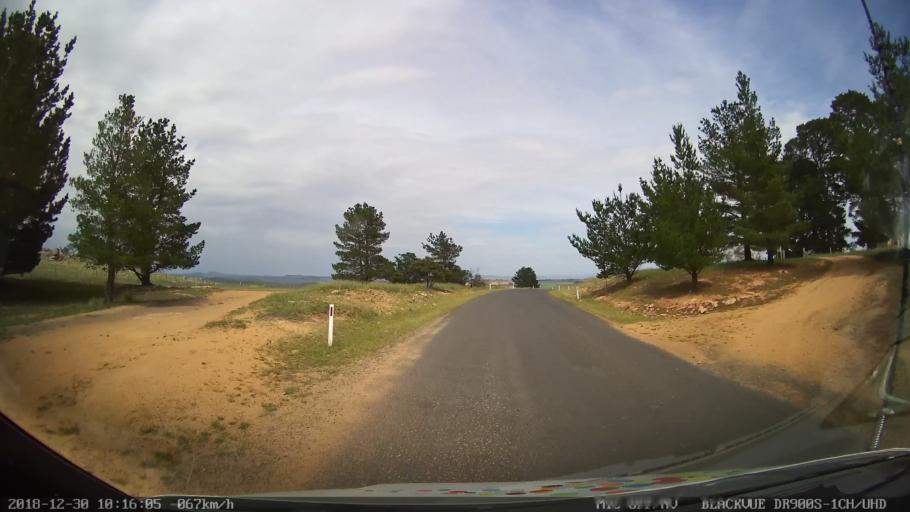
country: AU
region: New South Wales
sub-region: Snowy River
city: Berridale
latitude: -36.5474
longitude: 149.0394
